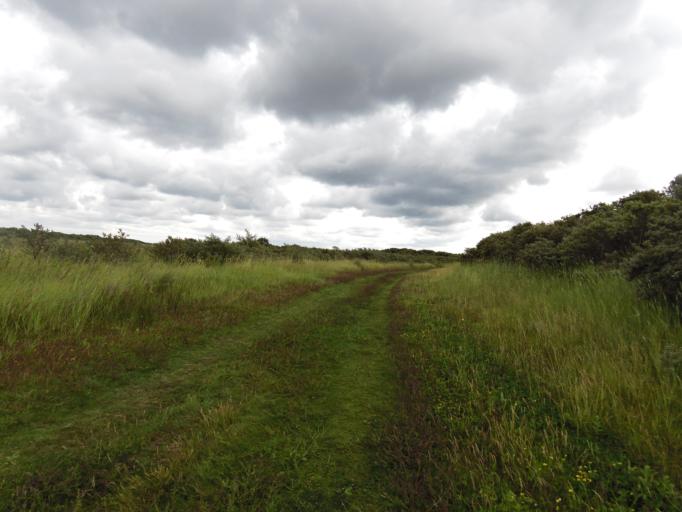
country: NL
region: South Holland
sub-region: Gemeente Goeree-Overflakkee
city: Goedereede
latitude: 51.8418
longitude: 3.9912
